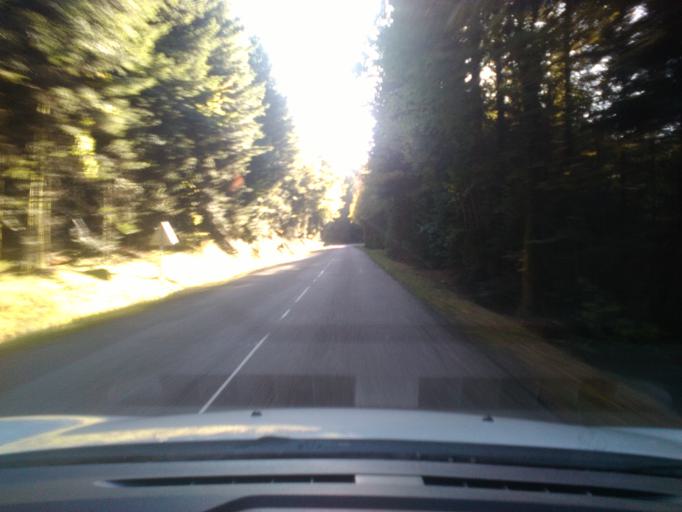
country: FR
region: Lorraine
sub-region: Departement des Vosges
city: Etival-Clairefontaine
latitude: 48.3026
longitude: 6.7994
